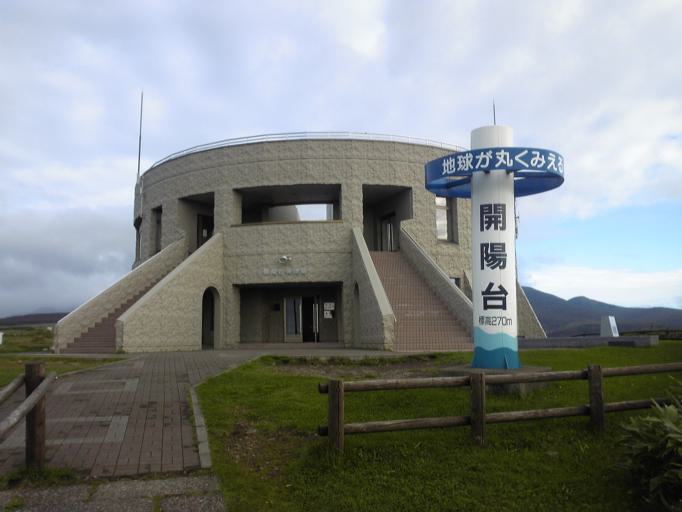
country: JP
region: Hokkaido
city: Shibetsu
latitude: 43.6126
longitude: 144.8710
